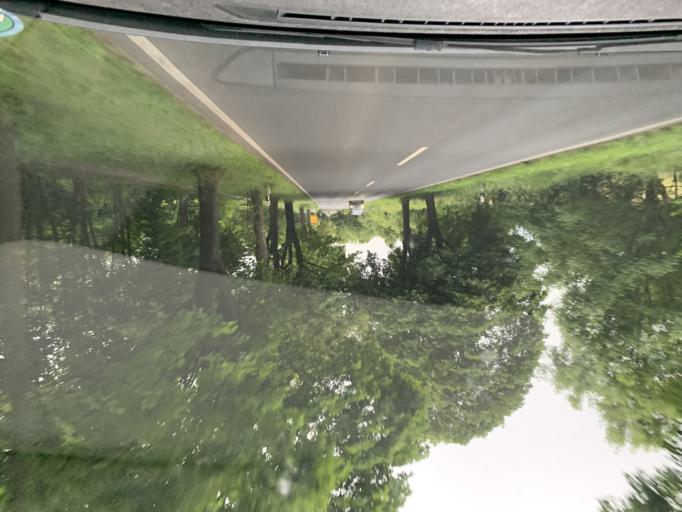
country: DE
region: North Rhine-Westphalia
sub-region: Regierungsbezirk Koln
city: Kerpen
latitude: 50.8789
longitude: 6.7075
